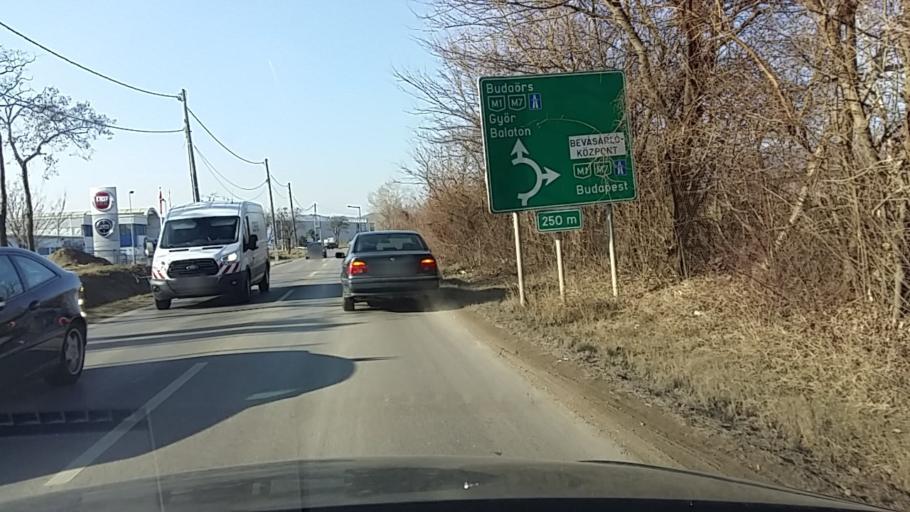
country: HU
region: Pest
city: Budaors
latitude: 47.4493
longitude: 18.9733
